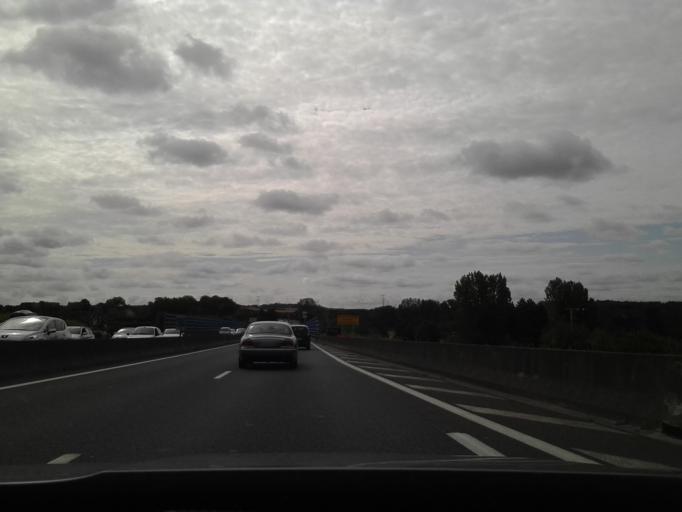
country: FR
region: Lower Normandy
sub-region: Departement du Calvados
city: Louvigny
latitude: 49.1419
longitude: -0.4013
